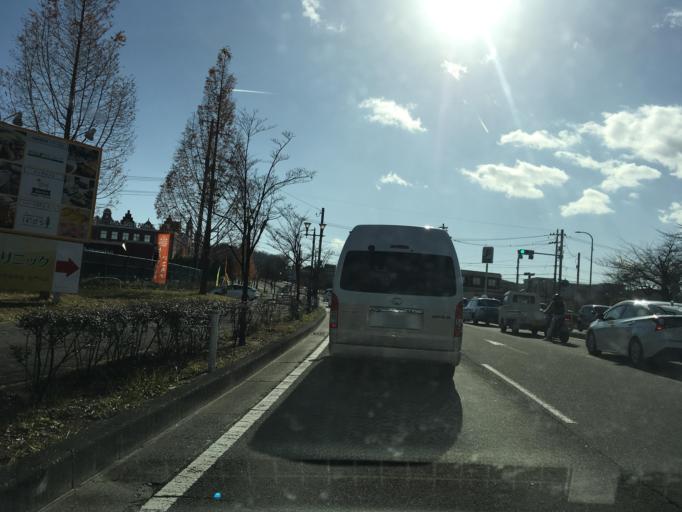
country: JP
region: Miyagi
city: Sendai
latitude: 38.2595
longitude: 140.7631
